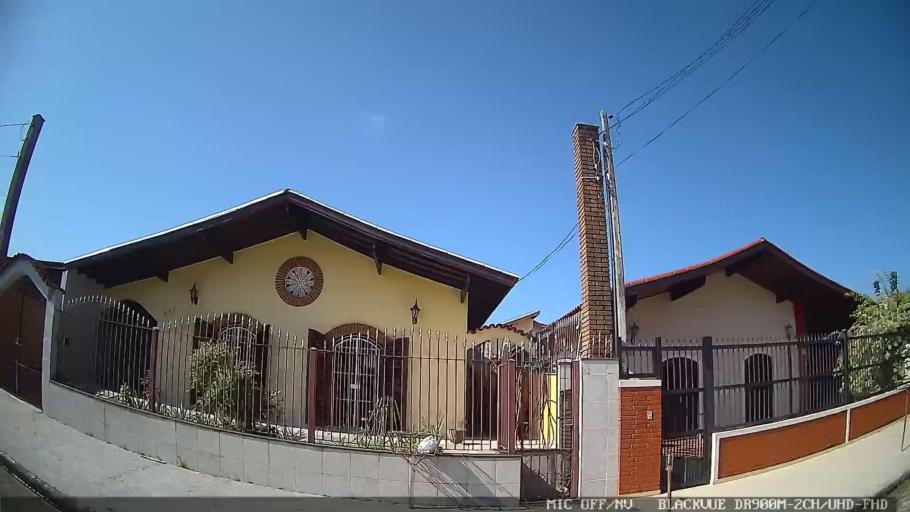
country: BR
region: Sao Paulo
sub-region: Peruibe
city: Peruibe
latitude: -24.2935
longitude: -46.9703
